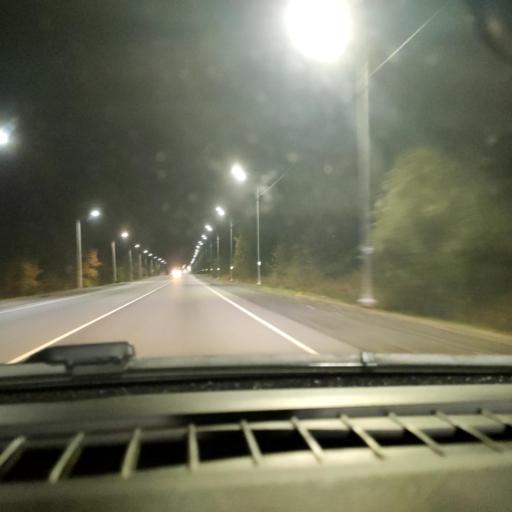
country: RU
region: Voronezj
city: Semiluki
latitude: 51.6476
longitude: 39.0266
